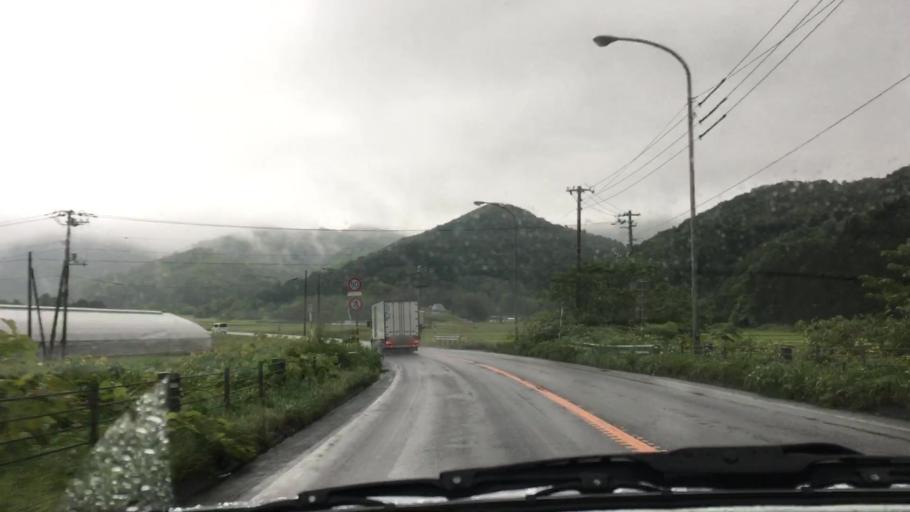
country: JP
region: Hokkaido
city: Niseko Town
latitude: 42.5999
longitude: 140.5880
